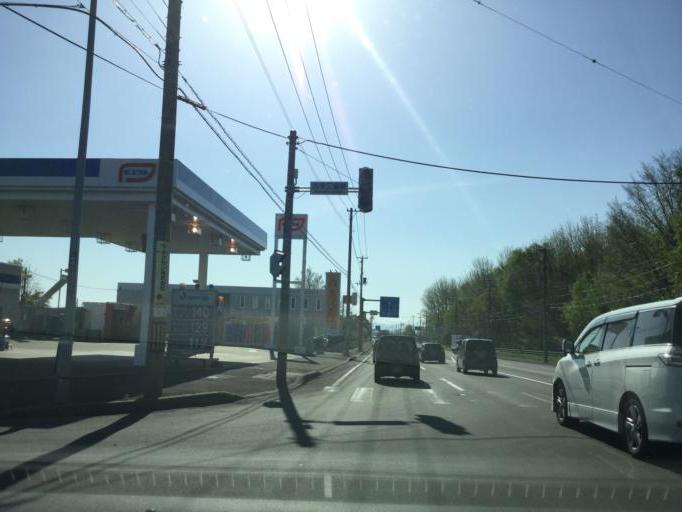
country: JP
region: Hokkaido
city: Kitahiroshima
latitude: 42.9986
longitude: 141.5563
